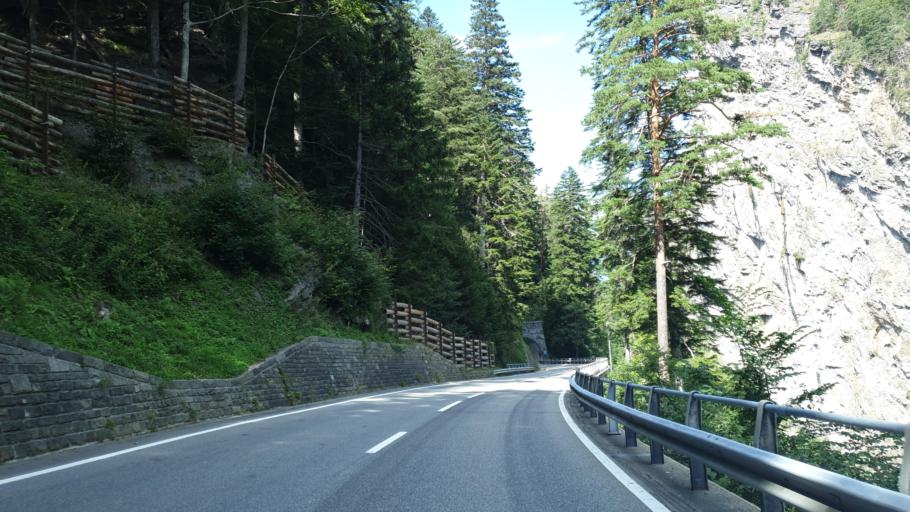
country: CH
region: Grisons
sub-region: Hinterrhein District
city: Thusis
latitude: 46.6876
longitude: 9.4441
